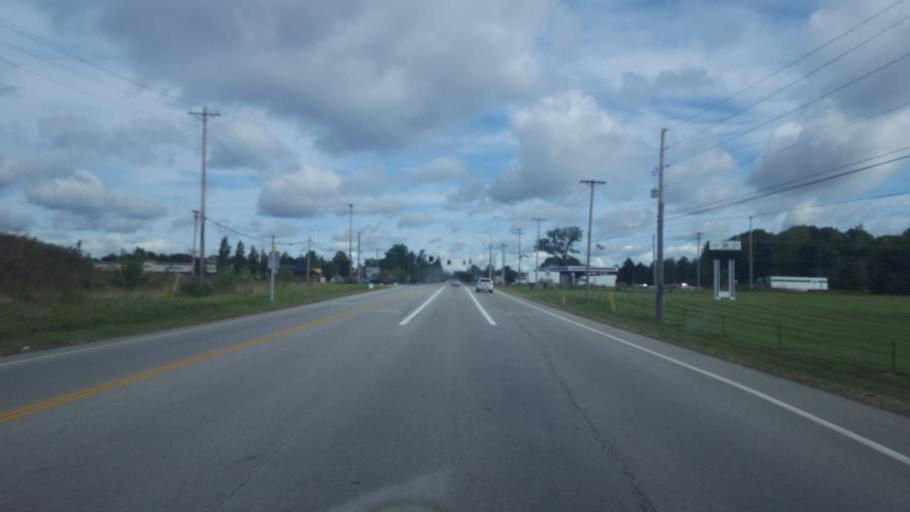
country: US
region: Ohio
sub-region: Lorain County
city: Oberlin
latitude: 41.2641
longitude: -82.2174
